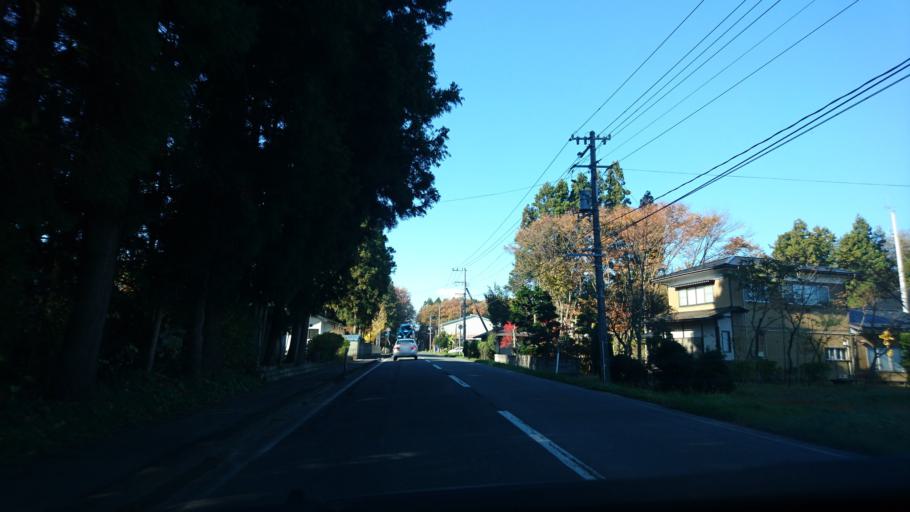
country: JP
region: Iwate
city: Mizusawa
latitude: 39.1297
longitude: 141.0371
